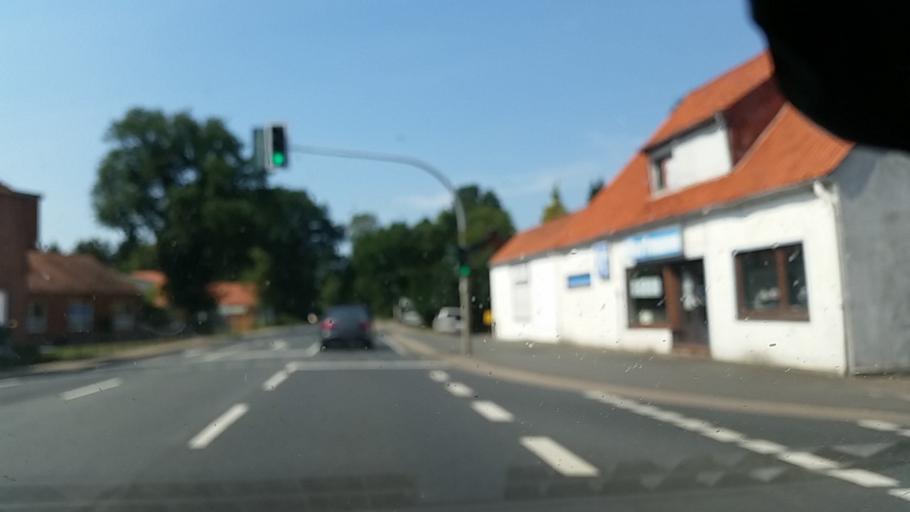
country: DE
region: Lower Saxony
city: Ottersberg
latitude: 53.0711
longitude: 9.1667
